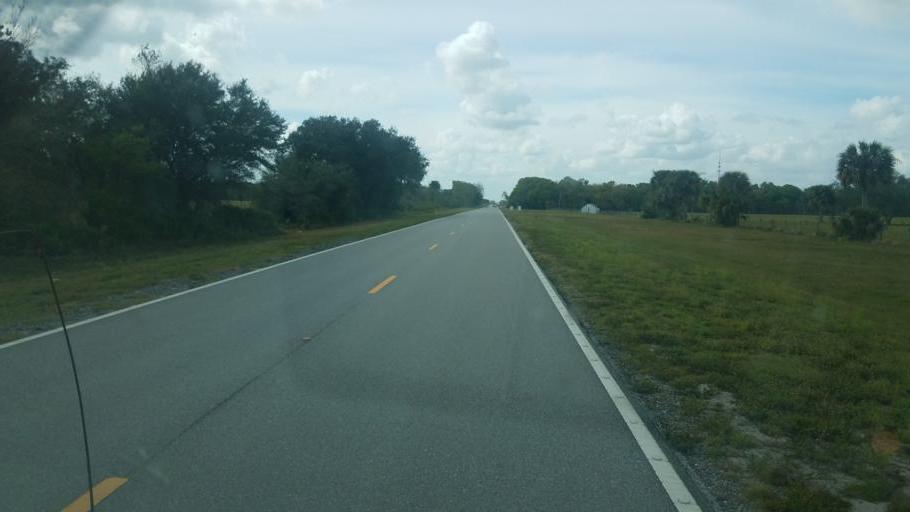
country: US
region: Florida
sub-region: Okeechobee County
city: Cypress Quarters
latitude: 27.4494
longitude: -80.7510
